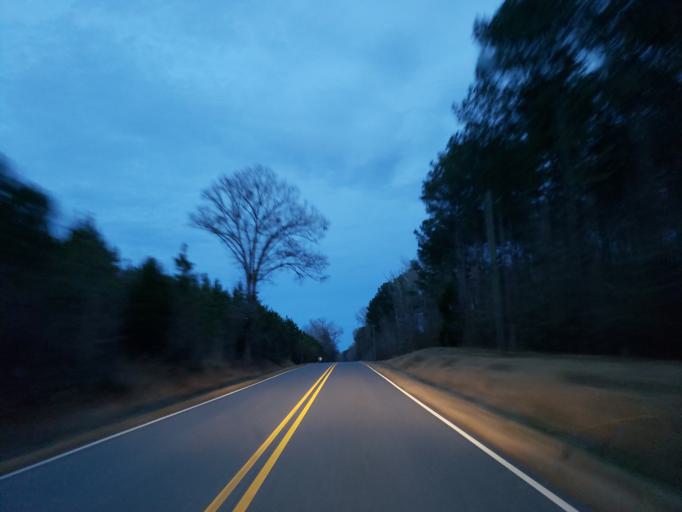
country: US
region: Alabama
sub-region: Greene County
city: Eutaw
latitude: 32.9037
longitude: -88.0242
